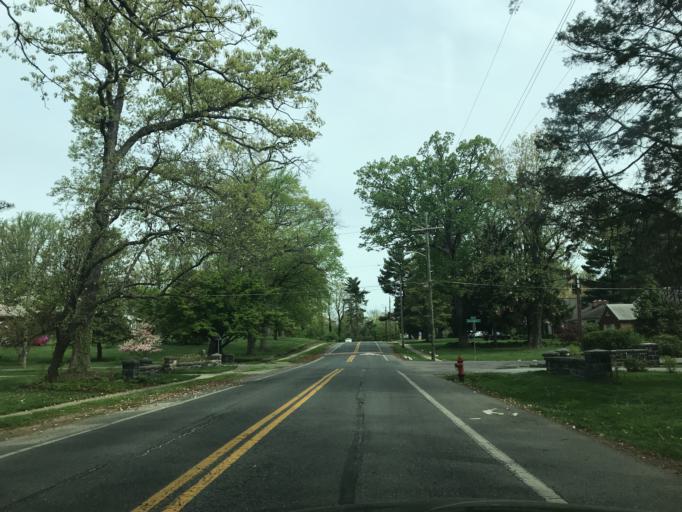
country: US
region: Maryland
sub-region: Baltimore County
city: Catonsville
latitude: 39.2658
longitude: -76.7474
